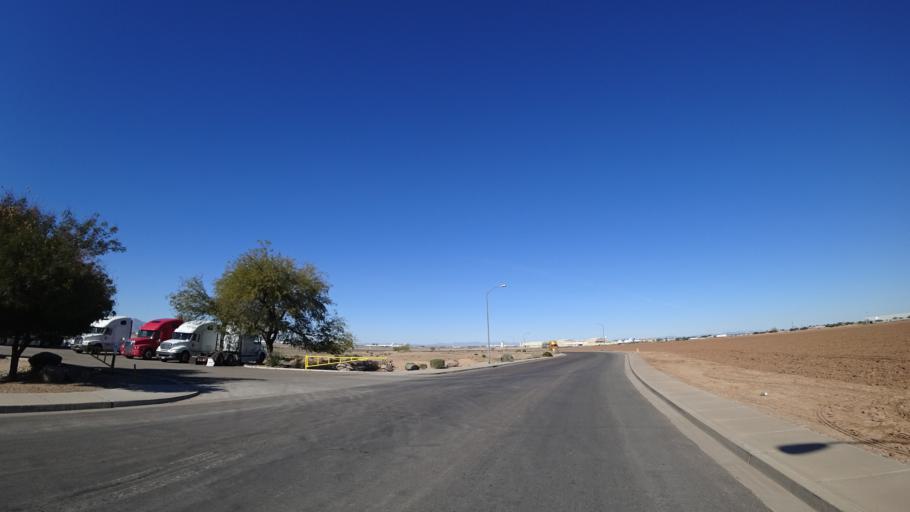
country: US
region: Arizona
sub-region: Maricopa County
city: Goodyear
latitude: 33.4148
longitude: -112.3705
